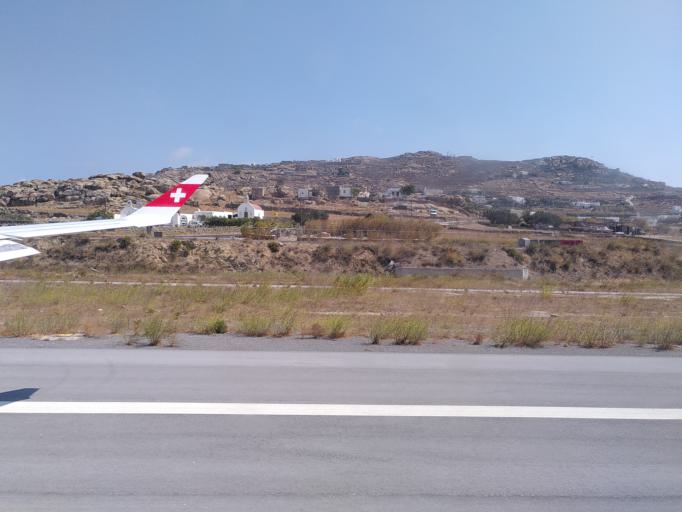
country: GR
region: South Aegean
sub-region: Nomos Kykladon
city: Mykonos
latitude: 37.4317
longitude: 25.3499
